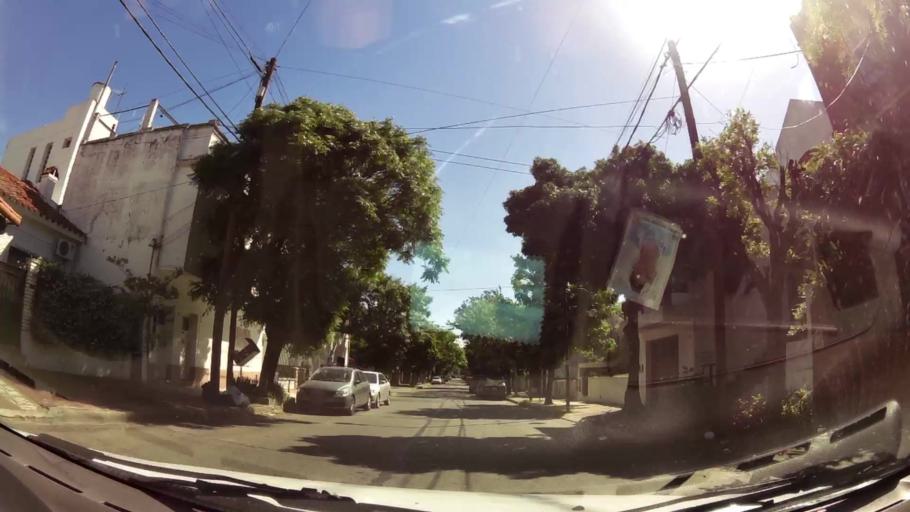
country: AR
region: Buenos Aires
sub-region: Partido de San Isidro
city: San Isidro
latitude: -34.4553
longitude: -58.5332
